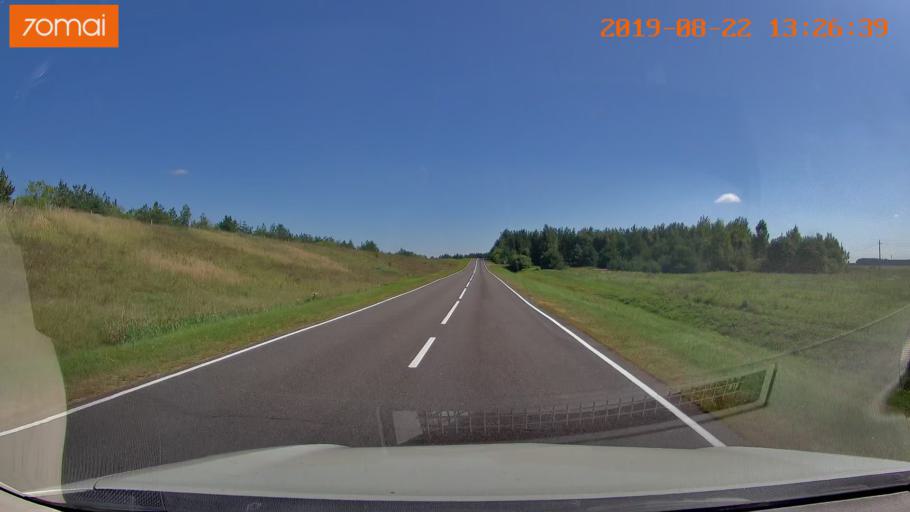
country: BY
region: Minsk
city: Staryya Darohi
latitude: 53.2086
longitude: 28.0670
